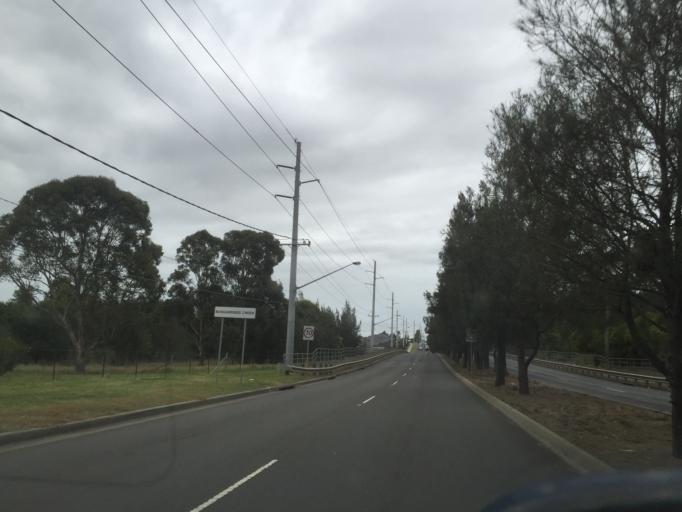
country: AU
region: New South Wales
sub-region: Blacktown
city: Doonside
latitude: -33.7846
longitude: 150.8724
